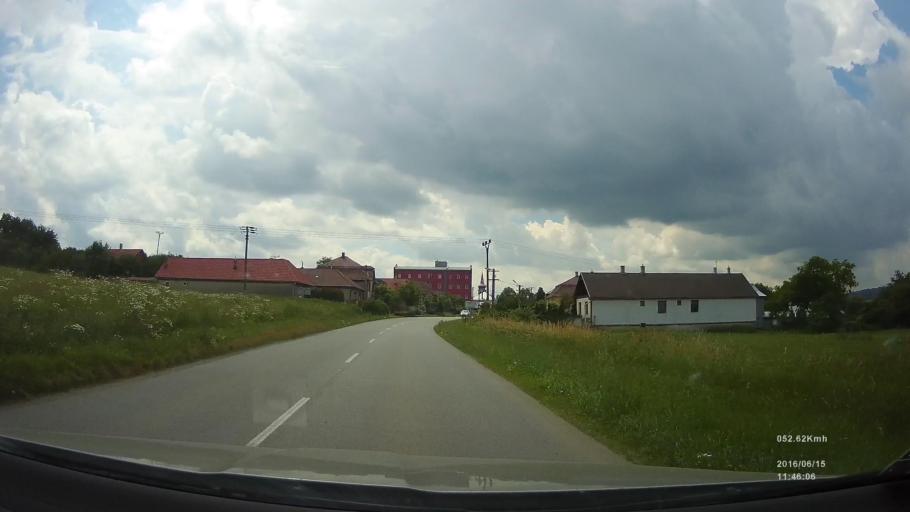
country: SK
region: Kosicky
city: Kosice
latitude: 48.7366
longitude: 21.3464
